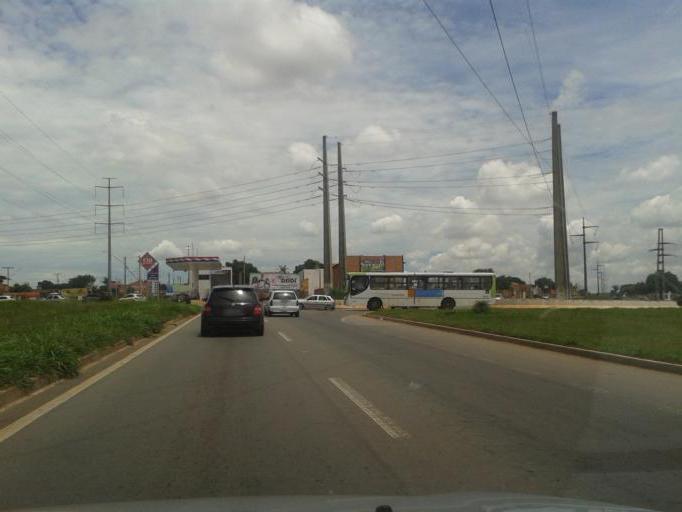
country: BR
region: Goias
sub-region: Aparecida De Goiania
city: Aparecida de Goiania
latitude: -16.7787
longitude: -49.2903
